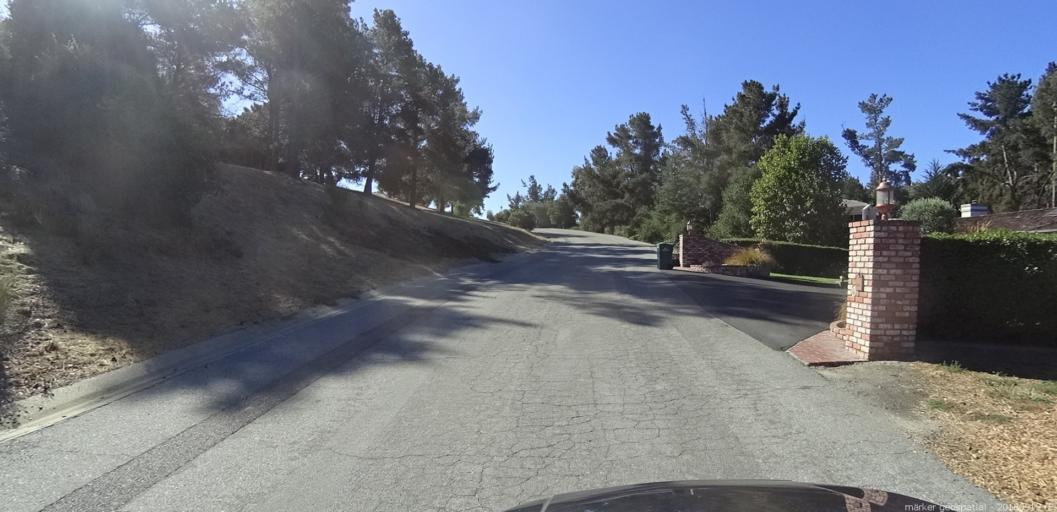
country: US
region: California
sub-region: Monterey County
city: Carmel Valley Village
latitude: 36.5670
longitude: -121.7347
